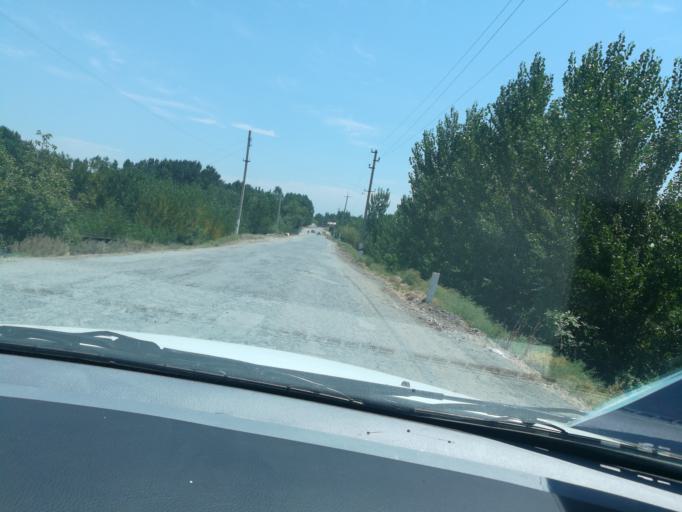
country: UZ
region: Namangan
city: Haqqulobod
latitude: 40.8989
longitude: 72.0041
